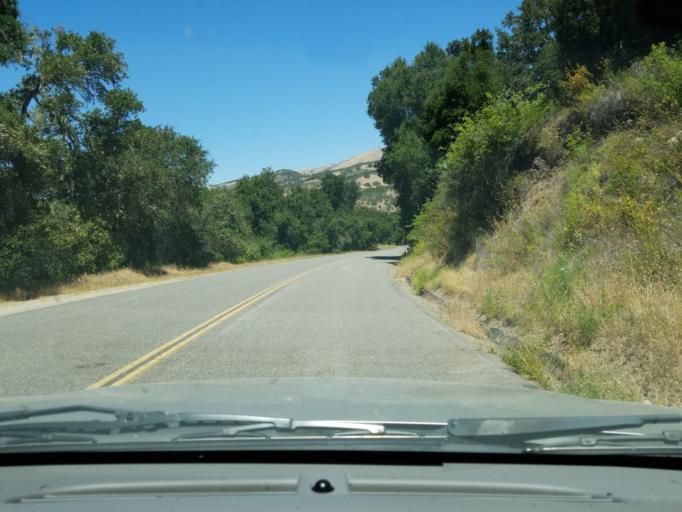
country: US
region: California
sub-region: Monterey County
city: Chualar
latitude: 36.4095
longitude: -121.5935
